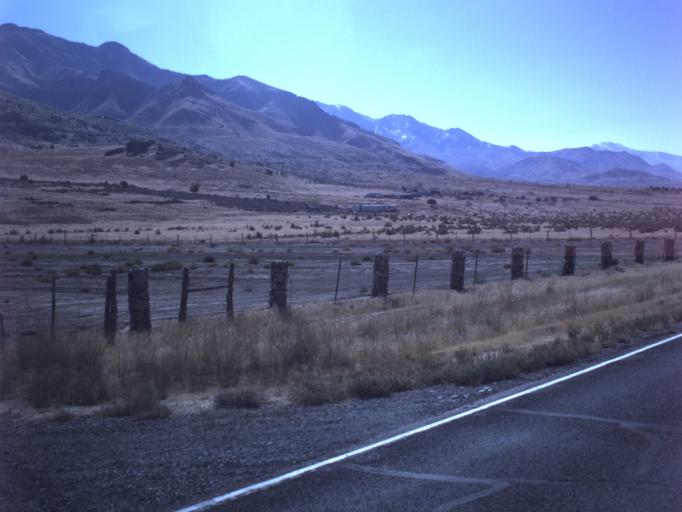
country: US
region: Utah
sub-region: Tooele County
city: Grantsville
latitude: 40.6850
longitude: -112.6700
